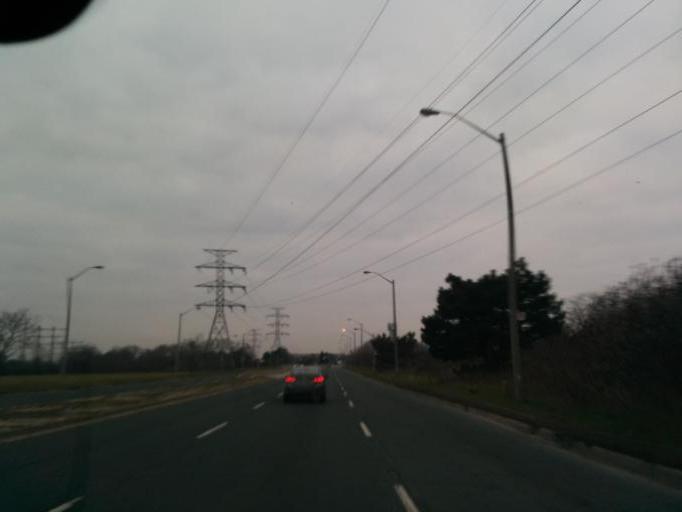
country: CA
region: Ontario
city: Etobicoke
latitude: 43.6118
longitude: -79.5638
